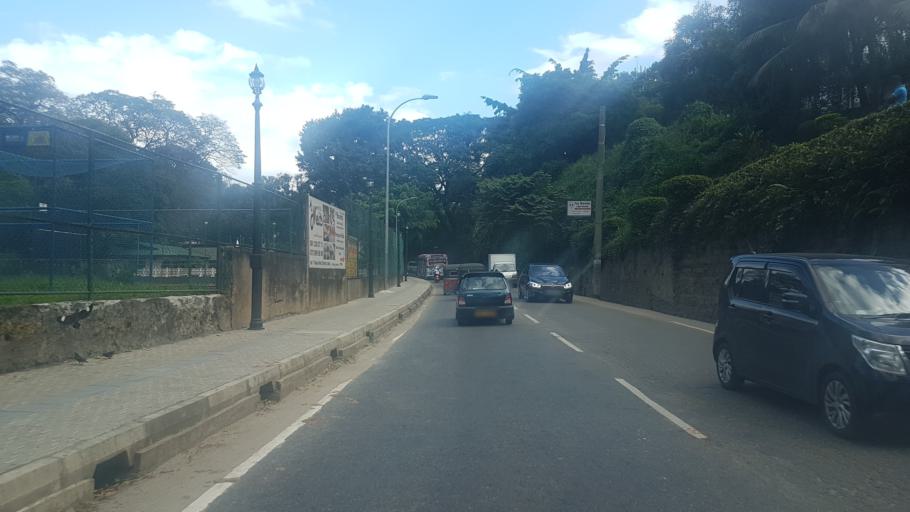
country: LK
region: Central
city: Kandy
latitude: 7.2874
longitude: 80.6463
